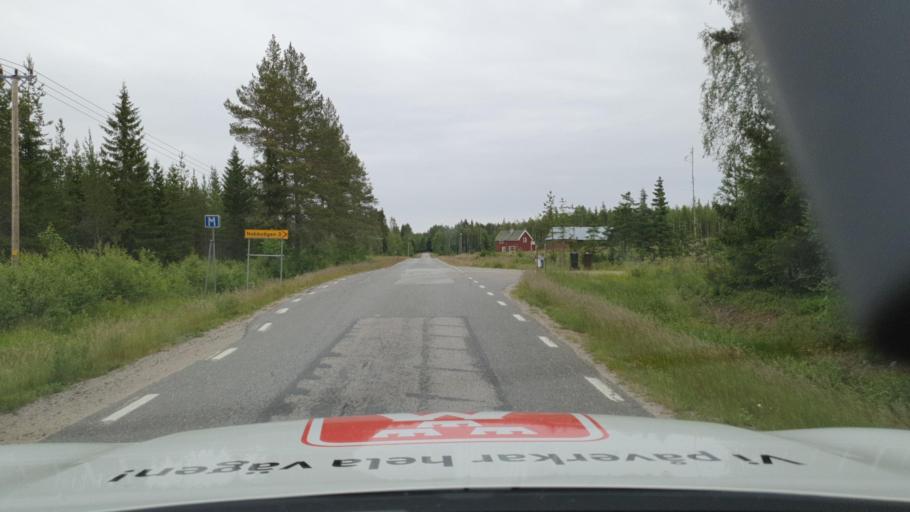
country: SE
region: Vaesterbotten
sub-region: Nordmalings Kommun
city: Nordmaling
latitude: 63.4852
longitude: 19.4449
